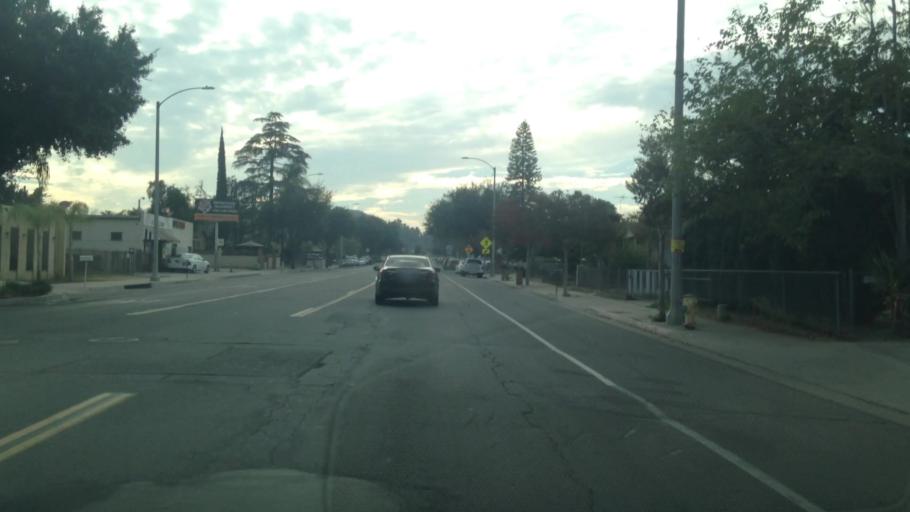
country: US
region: California
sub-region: Riverside County
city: Riverside
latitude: 33.9327
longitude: -117.4024
